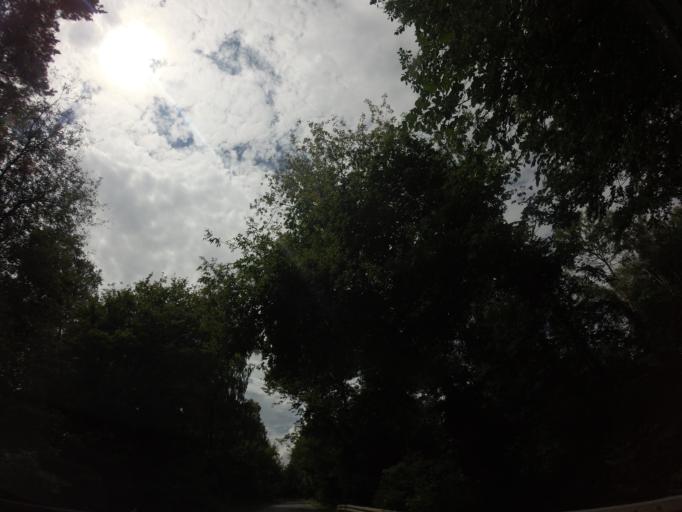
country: PL
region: Lublin Voivodeship
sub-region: Powiat opolski
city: Wilkow
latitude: 51.2736
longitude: 21.9239
